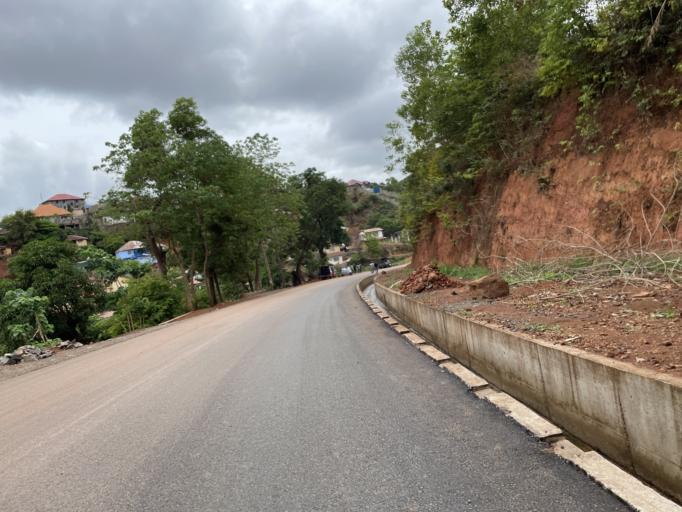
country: SL
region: Western Area
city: Hastings
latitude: 8.3988
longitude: -13.1536
